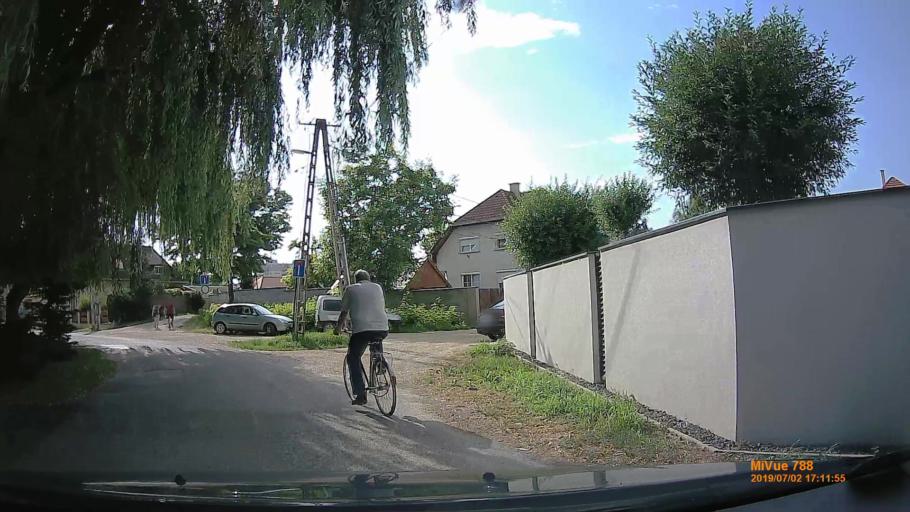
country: HU
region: Gyor-Moson-Sopron
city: Mosonmagyarovar
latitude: 47.8617
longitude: 17.2809
